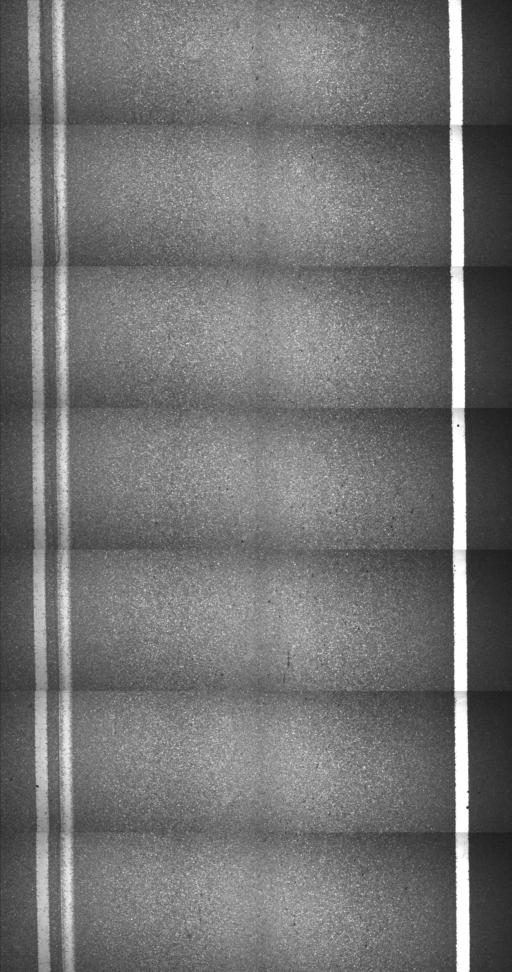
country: US
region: Vermont
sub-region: Chittenden County
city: Jericho
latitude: 44.5478
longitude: -73.0349
